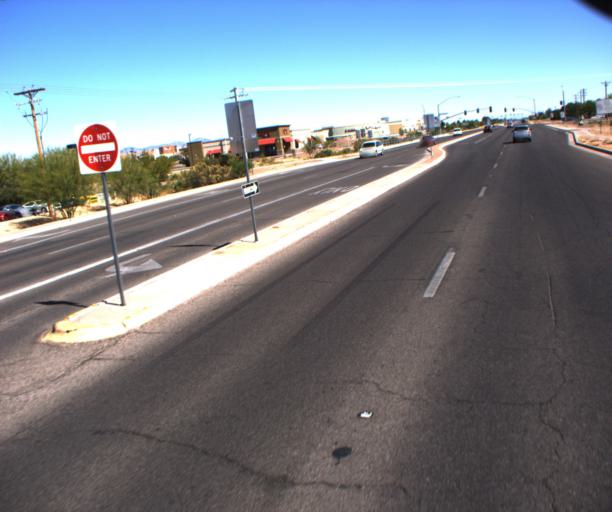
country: US
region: Arizona
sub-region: Cochise County
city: Sierra Vista
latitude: 31.5567
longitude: -110.2573
